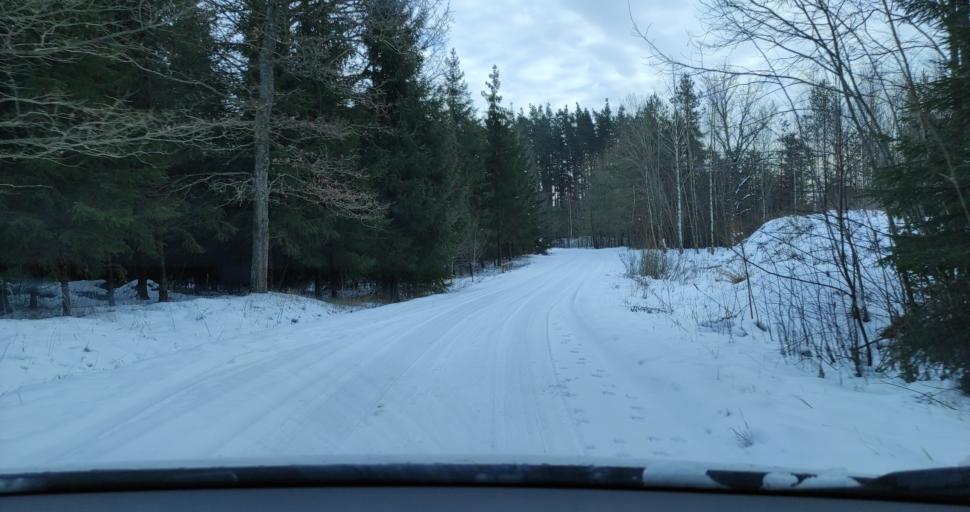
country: LV
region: Kuldigas Rajons
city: Kuldiga
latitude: 56.9432
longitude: 22.0388
